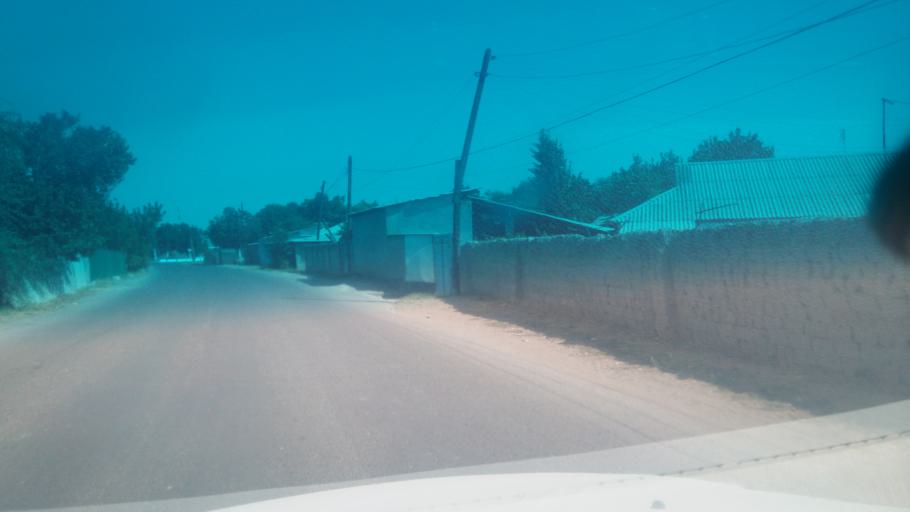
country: UZ
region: Sirdaryo
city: Sirdaryo
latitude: 40.8204
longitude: 68.6719
